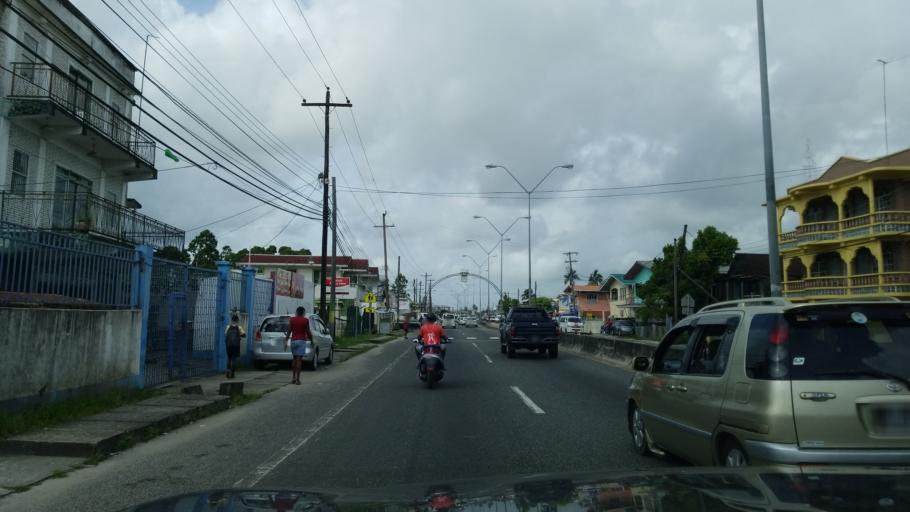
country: GY
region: Demerara-Mahaica
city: Georgetown
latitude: 6.7786
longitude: -58.1710
